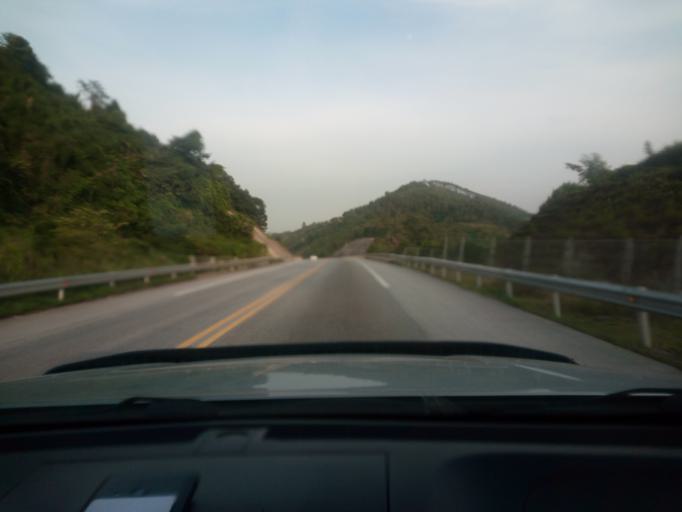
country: VN
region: Yen Bai
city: Co Phuc
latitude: 21.8885
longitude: 104.6523
